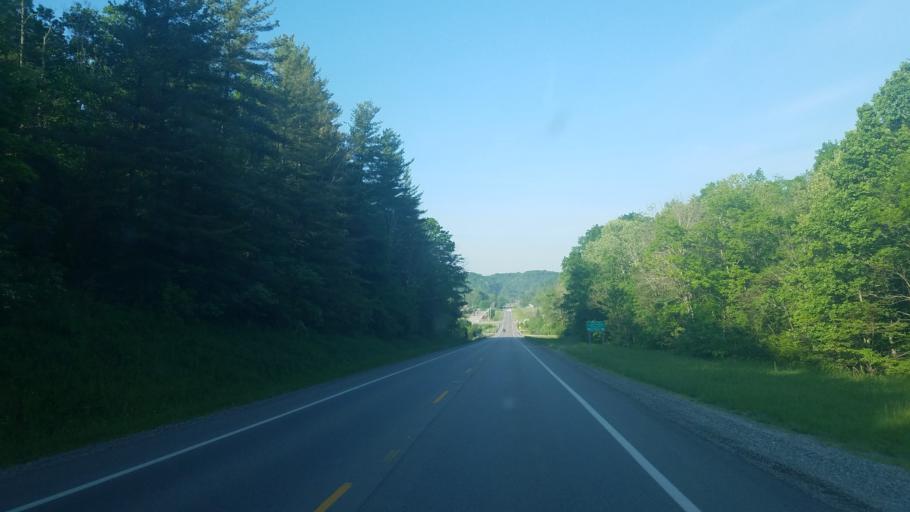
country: US
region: West Virginia
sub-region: Mason County
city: New Haven
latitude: 39.1273
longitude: -81.8778
